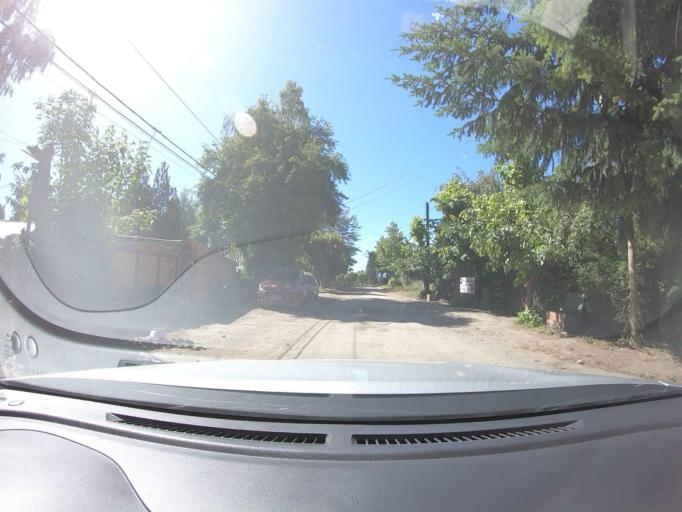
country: AR
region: Rio Negro
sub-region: Departamento de Bariloche
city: San Carlos de Bariloche
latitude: -41.1240
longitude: -71.3935
